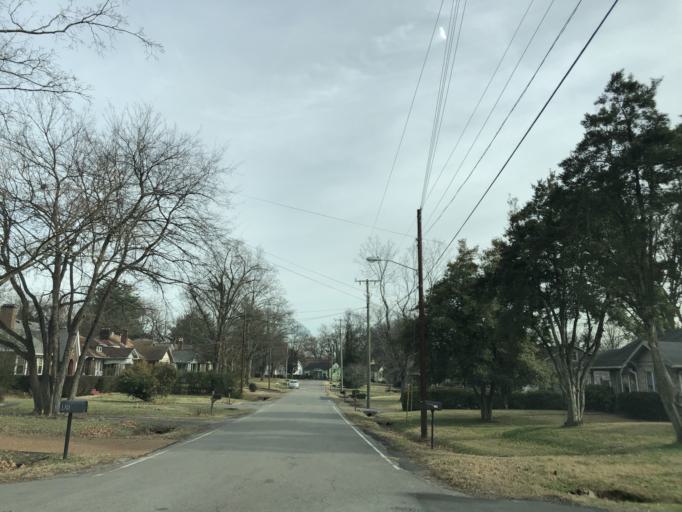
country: US
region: Tennessee
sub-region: Davidson County
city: Nashville
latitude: 36.2112
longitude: -86.7254
